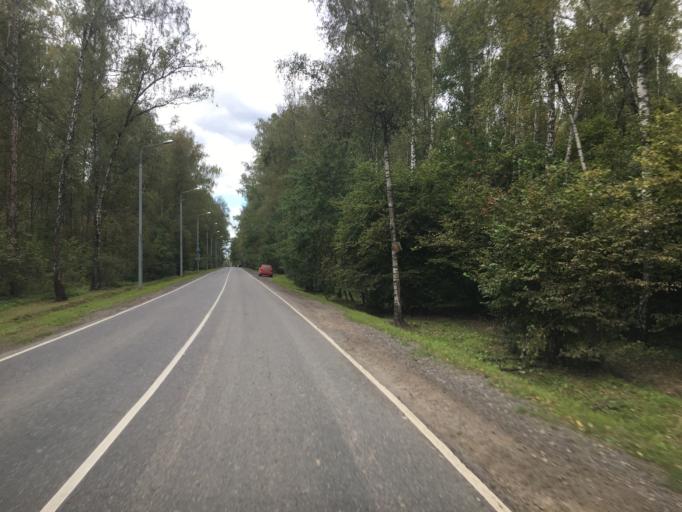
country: RU
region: Moskovskaya
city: Vatutinki
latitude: 55.4994
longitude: 37.3845
